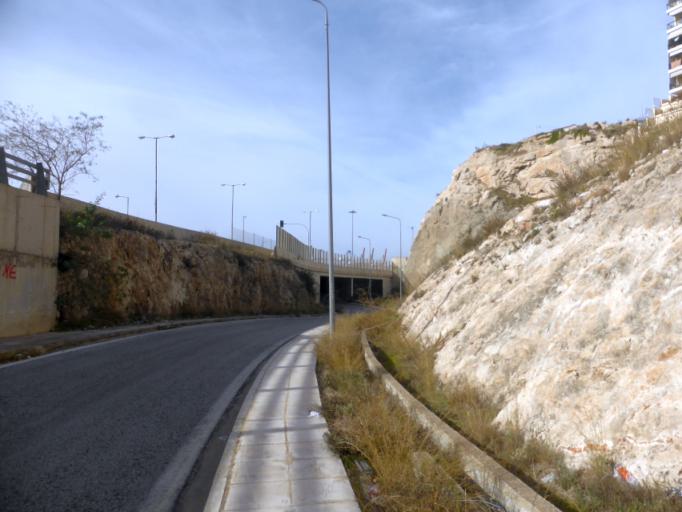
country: GR
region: Attica
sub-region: Nomos Piraios
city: Drapetsona
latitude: 37.9492
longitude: 23.6108
